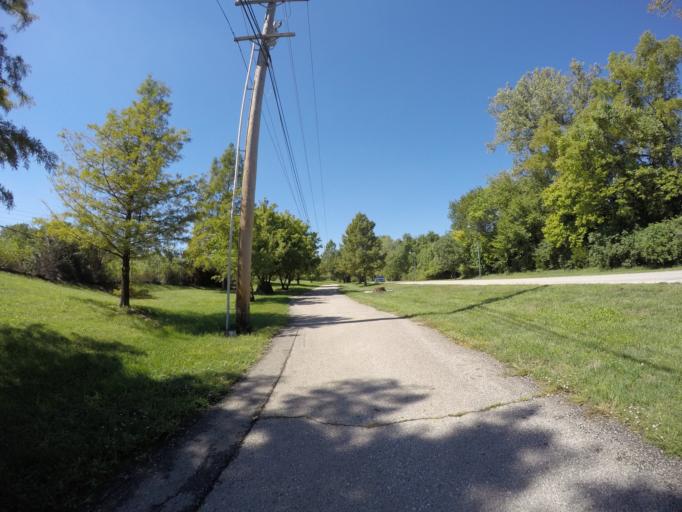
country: US
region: Kansas
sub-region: Johnson County
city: Leawood
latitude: 38.9321
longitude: -94.6254
